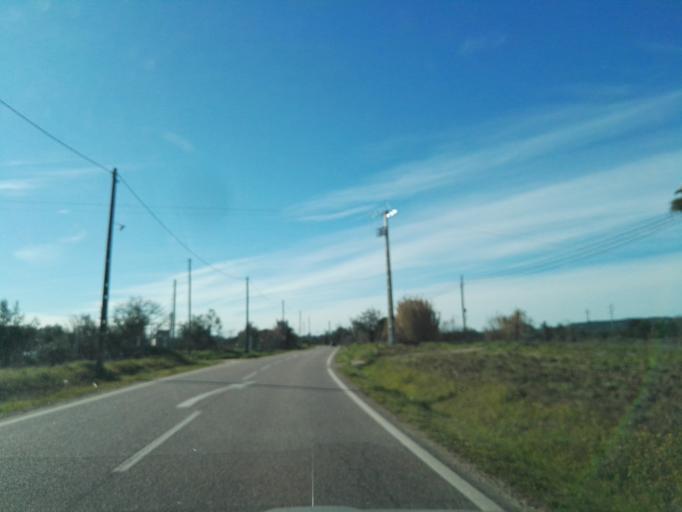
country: PT
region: Portalegre
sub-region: Gaviao
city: Gaviao
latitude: 39.4611
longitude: -8.0236
